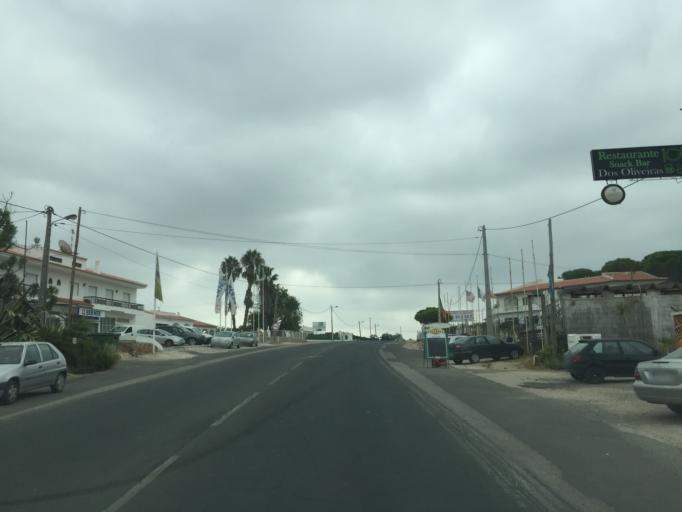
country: PT
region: Faro
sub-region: Loule
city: Almancil
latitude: 37.0794
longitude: -7.9943
